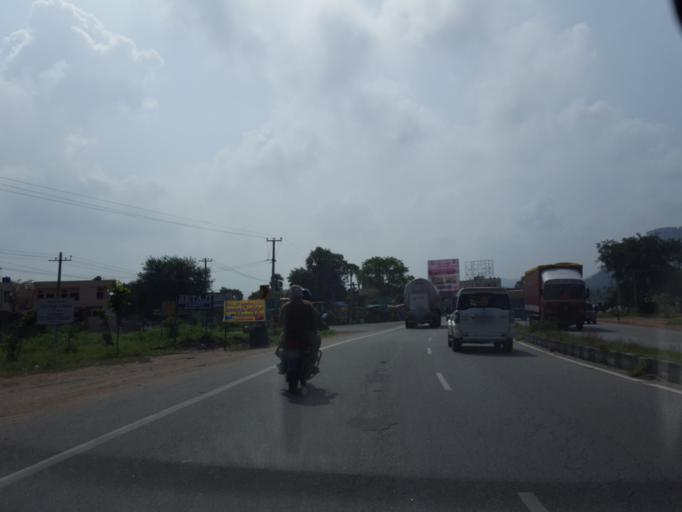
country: IN
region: Telangana
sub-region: Rangareddi
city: Ghatkesar
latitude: 17.3022
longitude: 78.7385
